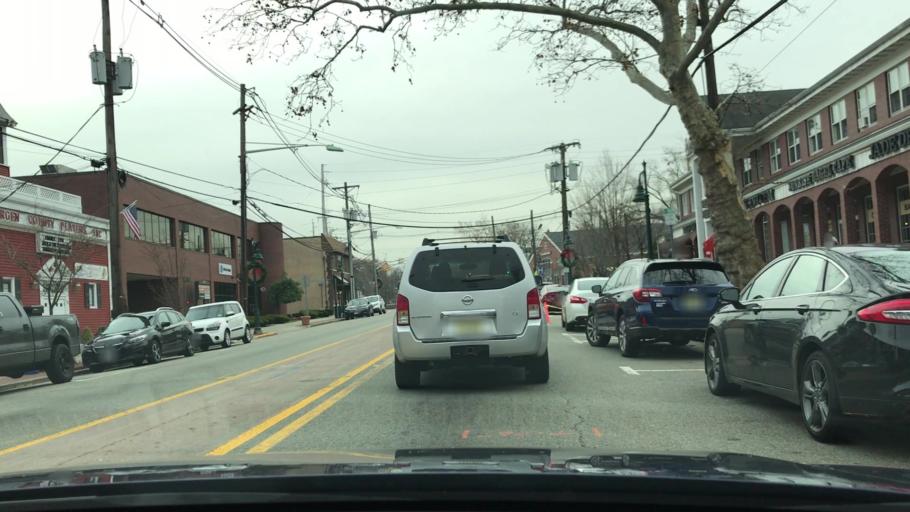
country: US
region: New Jersey
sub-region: Bergen County
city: Oradell
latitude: 40.9510
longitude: -74.0322
